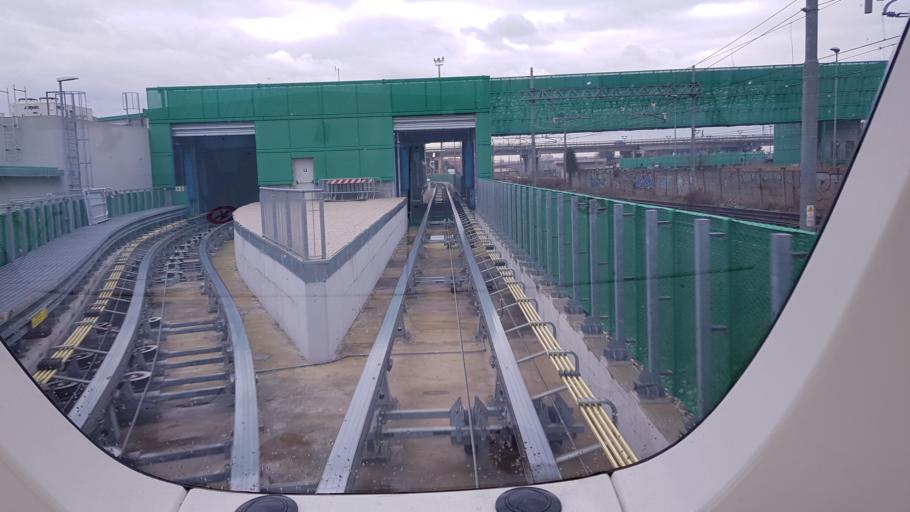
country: IT
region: Tuscany
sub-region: Province of Pisa
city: Pisa
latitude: 43.7019
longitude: 10.3914
